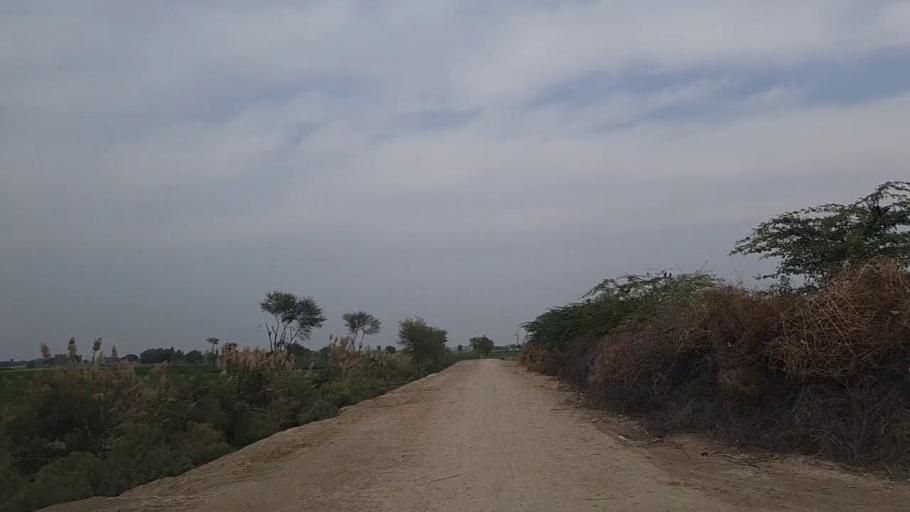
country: PK
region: Sindh
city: Daur
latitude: 26.4458
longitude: 68.4788
